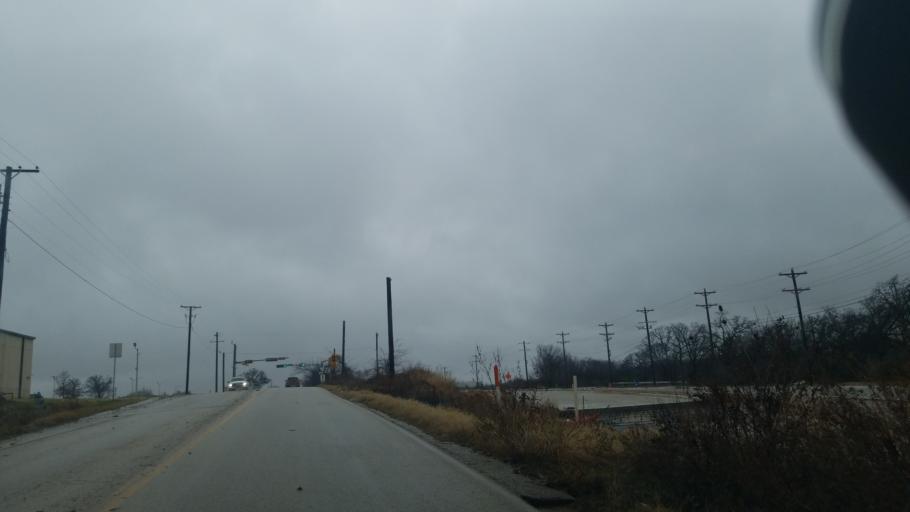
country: US
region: Texas
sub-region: Denton County
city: Corinth
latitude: 33.1964
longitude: -97.0847
